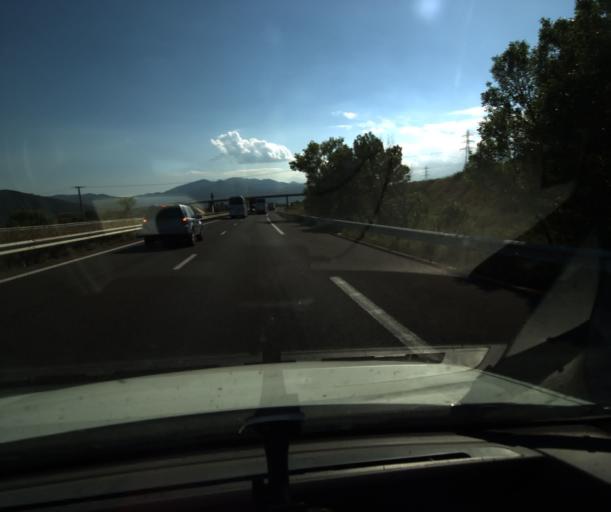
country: FR
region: Languedoc-Roussillon
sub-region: Departement des Pyrenees-Orientales
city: el Volo
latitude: 42.5424
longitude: 2.8460
